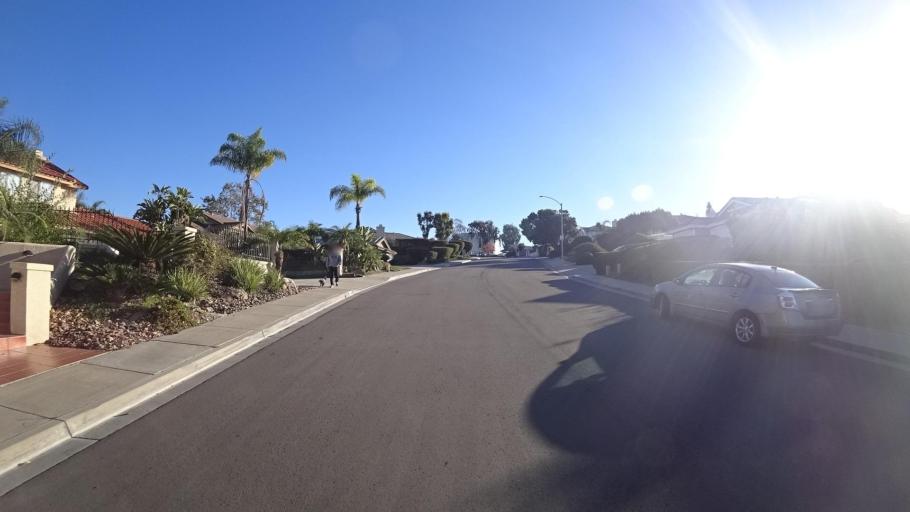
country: US
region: California
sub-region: San Diego County
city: Bonita
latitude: 32.6727
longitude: -117.0376
